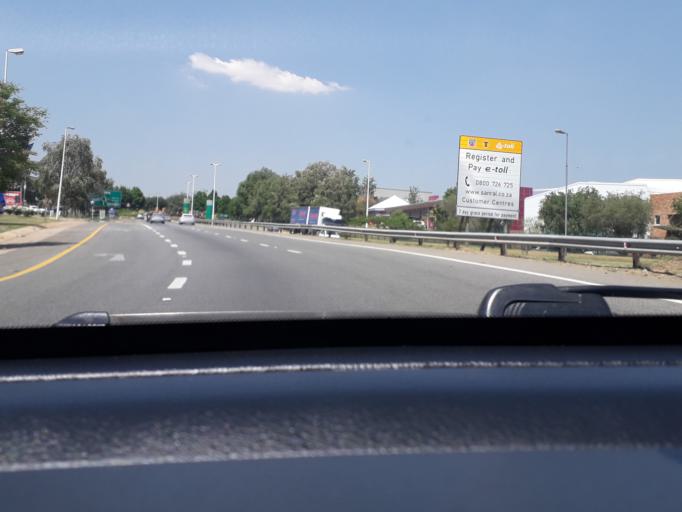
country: ZA
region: Gauteng
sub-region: City of Johannesburg Metropolitan Municipality
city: Modderfontein
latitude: -26.1162
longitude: 28.1340
